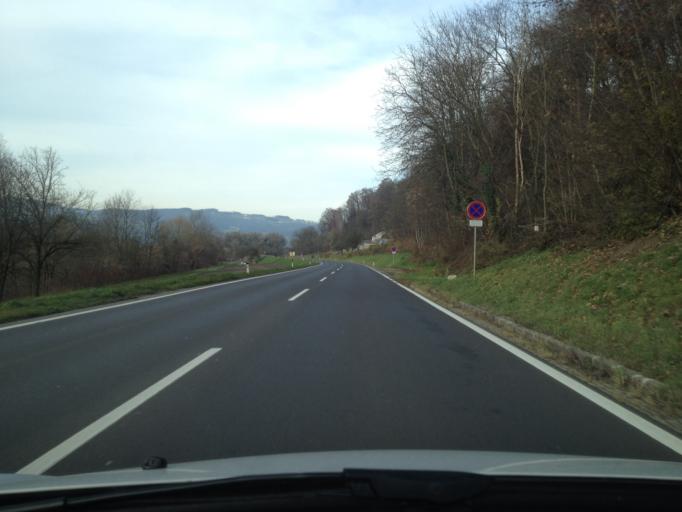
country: AT
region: Upper Austria
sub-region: Politischer Bezirk Urfahr-Umgebung
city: Steyregg
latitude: 48.3090
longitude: 14.3365
